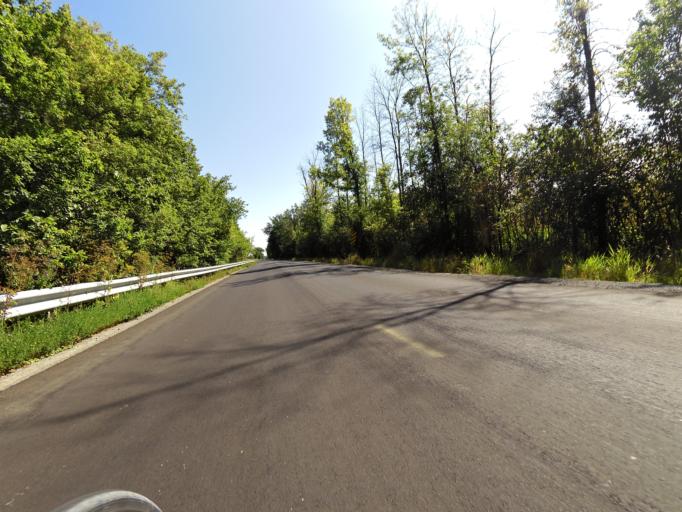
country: CA
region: Ontario
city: Bells Corners
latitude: 45.3714
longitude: -75.9298
